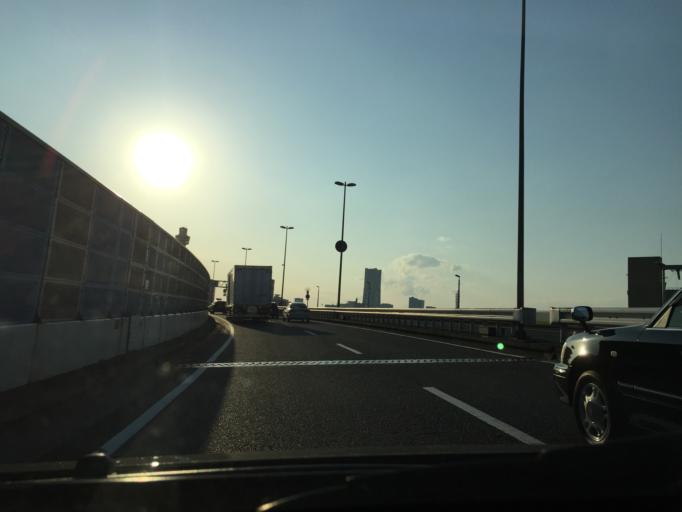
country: JP
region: Kanagawa
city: Yokohama
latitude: 35.4429
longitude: 139.6572
